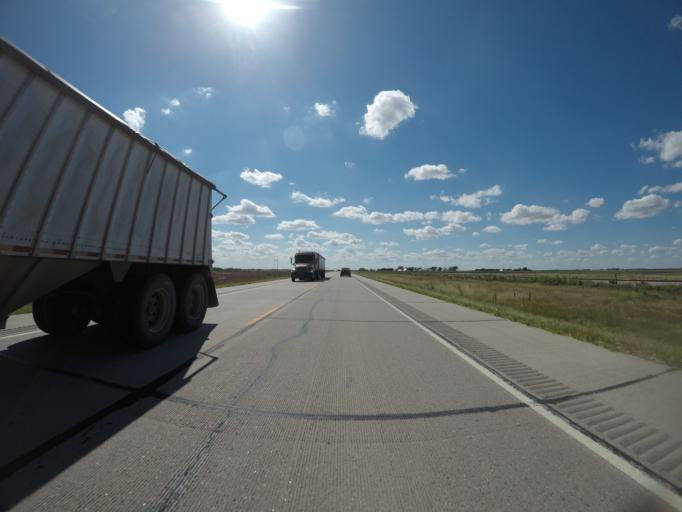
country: US
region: Colorado
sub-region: Phillips County
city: Holyoke
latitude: 40.5919
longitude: -102.3501
